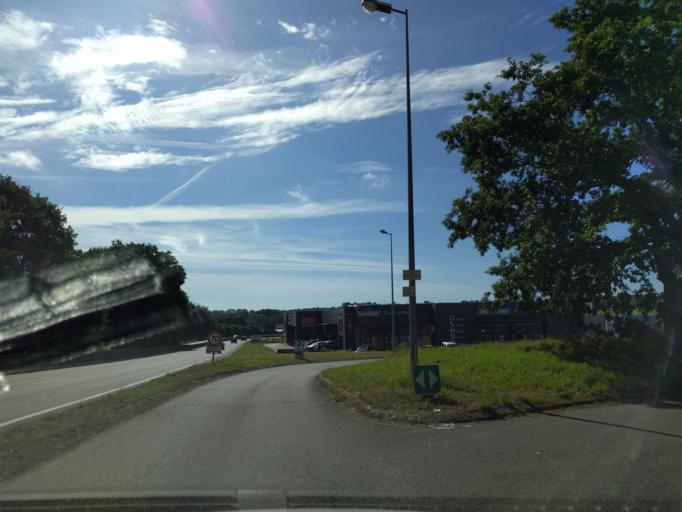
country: FR
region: Brittany
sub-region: Departement du Finistere
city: Quimper
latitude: 48.0005
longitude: -4.0766
